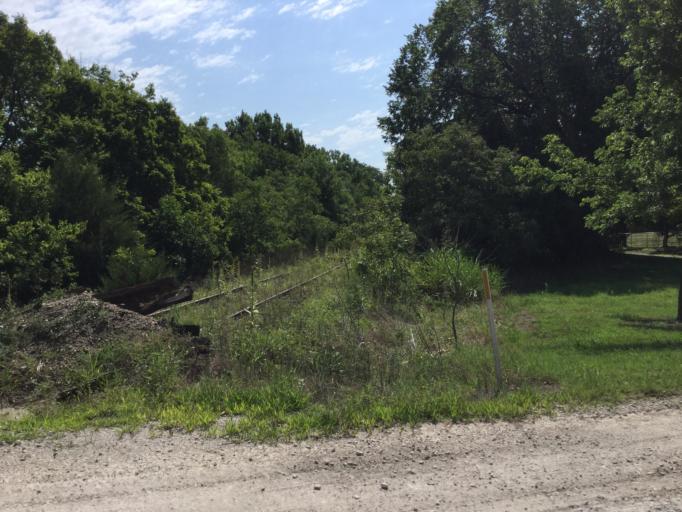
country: US
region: Kansas
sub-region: Montgomery County
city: Coffeyville
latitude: 37.0290
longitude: -95.5684
